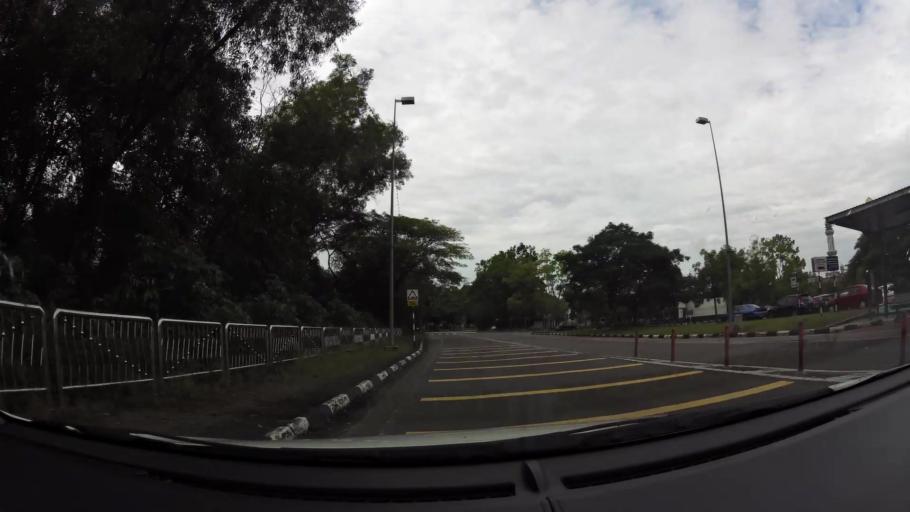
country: BN
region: Brunei and Muara
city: Bandar Seri Begawan
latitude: 4.8994
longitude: 114.9243
